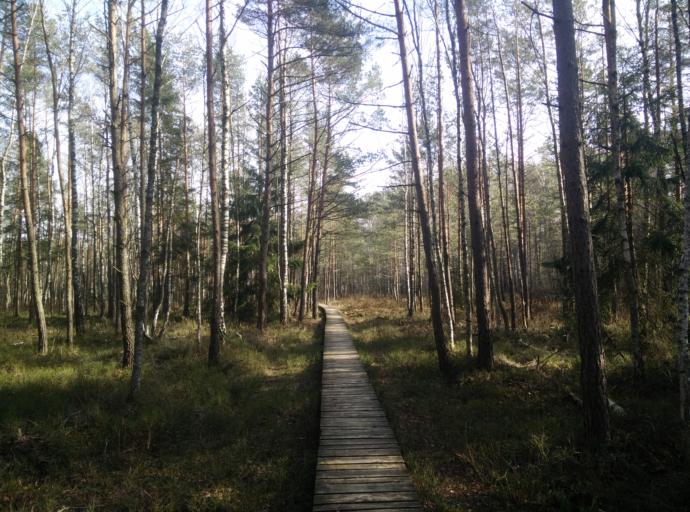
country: LT
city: Trakai
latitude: 54.6381
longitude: 24.9698
